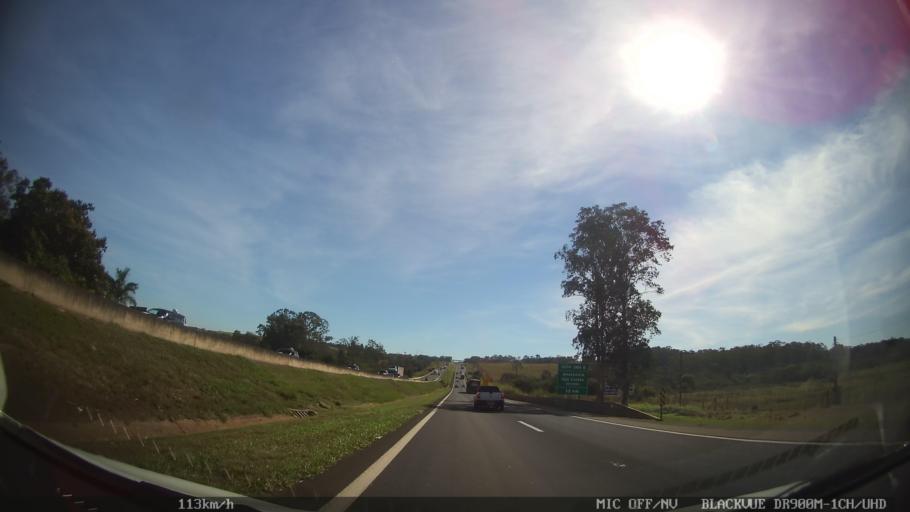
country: BR
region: Sao Paulo
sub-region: Pirassununga
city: Pirassununga
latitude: -22.0519
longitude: -47.4288
